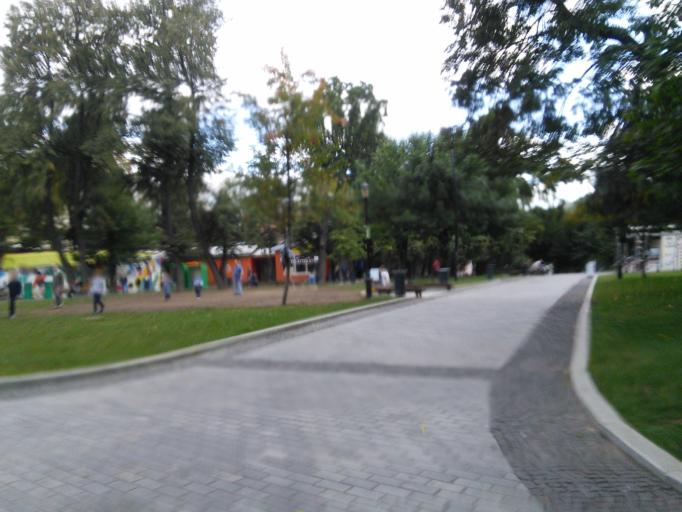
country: RU
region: Moscow
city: Taganskiy
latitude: 55.7679
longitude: 37.6595
